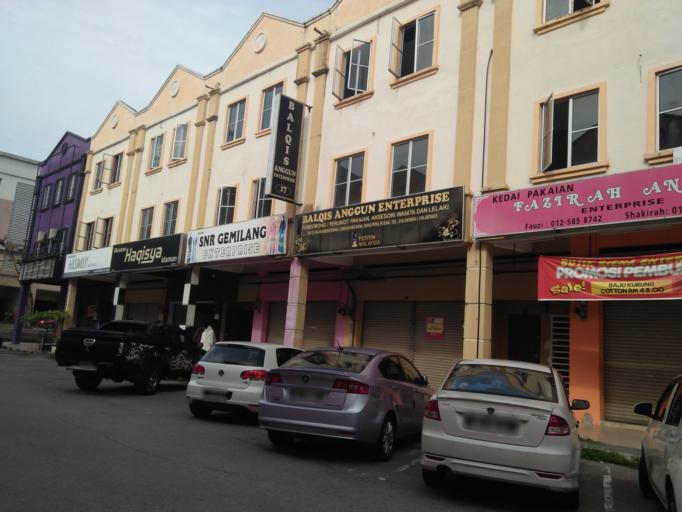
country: MY
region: Perak
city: Ipoh
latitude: 4.6018
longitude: 101.0938
